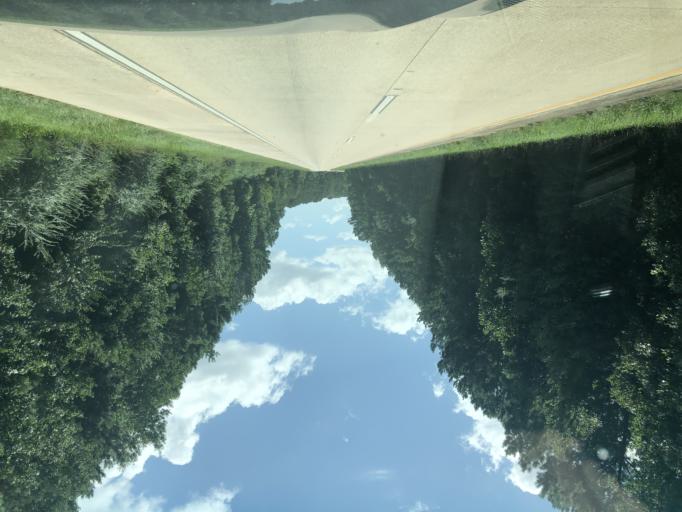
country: US
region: Georgia
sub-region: Troup County
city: Hogansville
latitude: 33.0715
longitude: -84.9330
